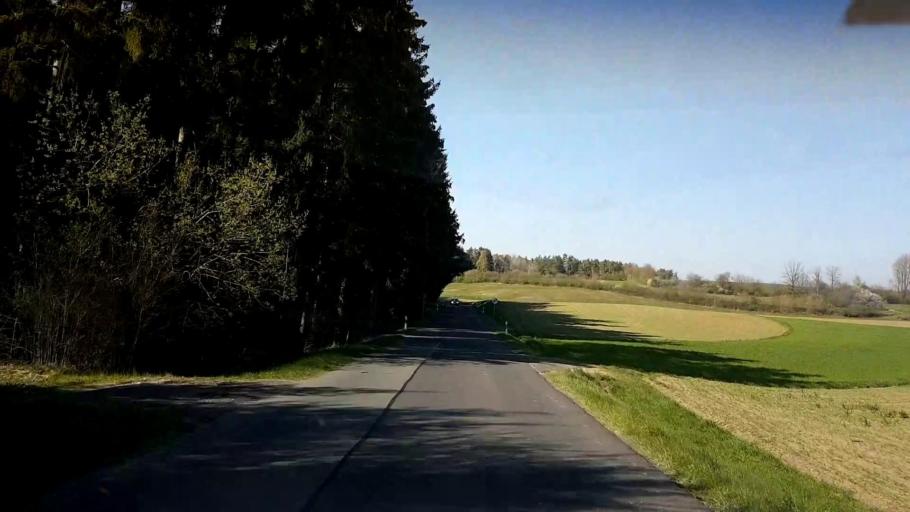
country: DE
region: Bavaria
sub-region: Upper Franconia
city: Waischenfeld
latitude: 49.8245
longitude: 11.3533
